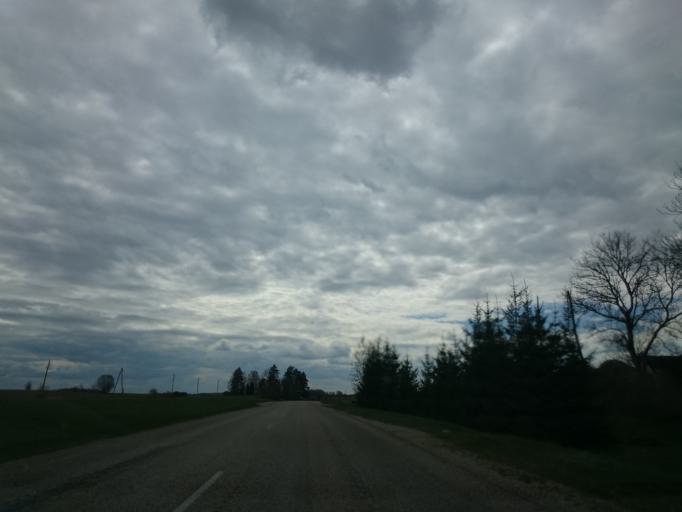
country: LV
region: Aizpute
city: Aizpute
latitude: 56.7780
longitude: 21.6356
